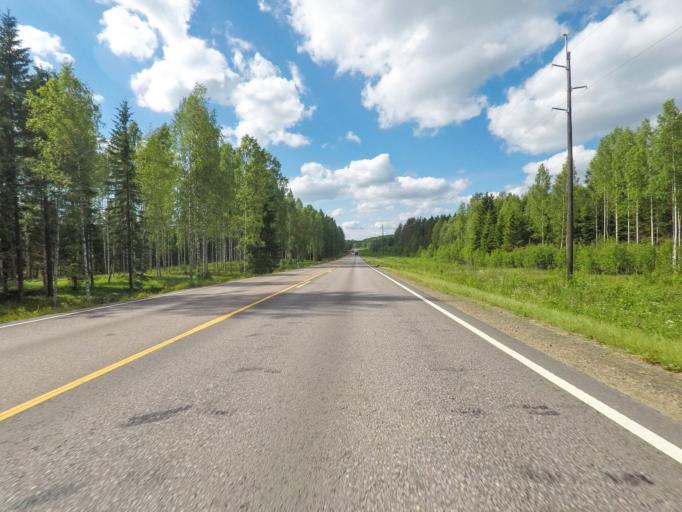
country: FI
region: Southern Savonia
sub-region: Savonlinna
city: Kerimaeki
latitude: 61.8547
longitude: 29.1653
